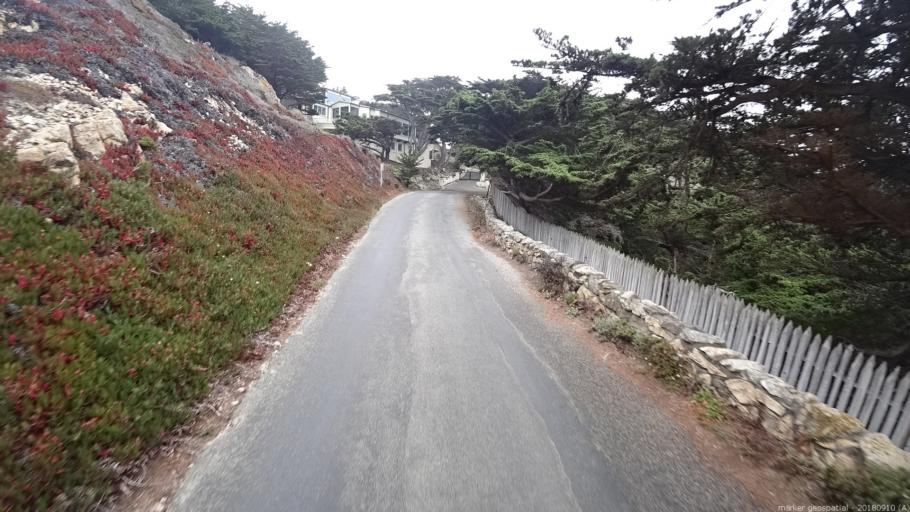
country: US
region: California
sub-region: Monterey County
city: Carmel-by-the-Sea
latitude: 36.4923
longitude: -121.9419
